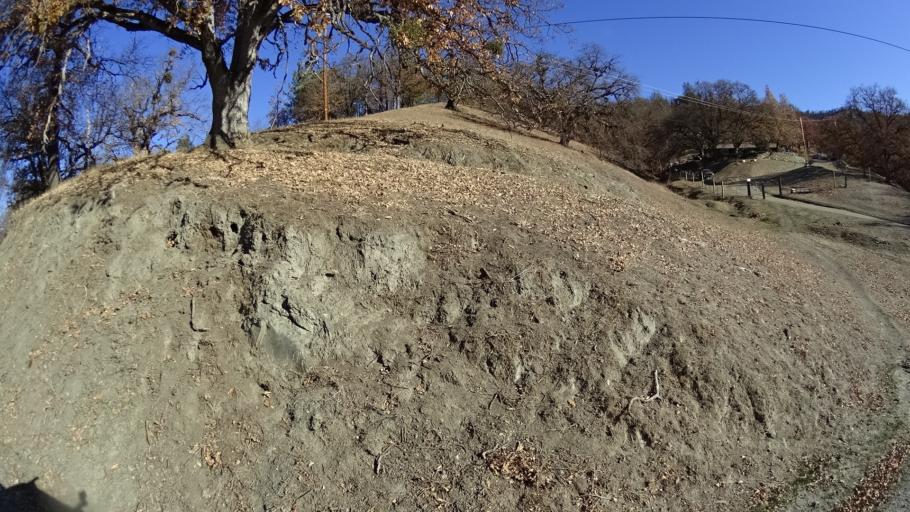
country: US
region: California
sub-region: Siskiyou County
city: Happy Camp
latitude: 41.8332
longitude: -123.0055
